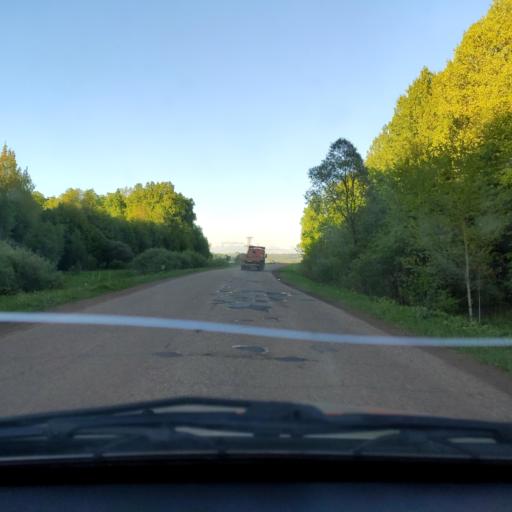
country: RU
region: Bashkortostan
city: Blagoveshchensk
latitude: 55.0414
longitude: 56.1371
